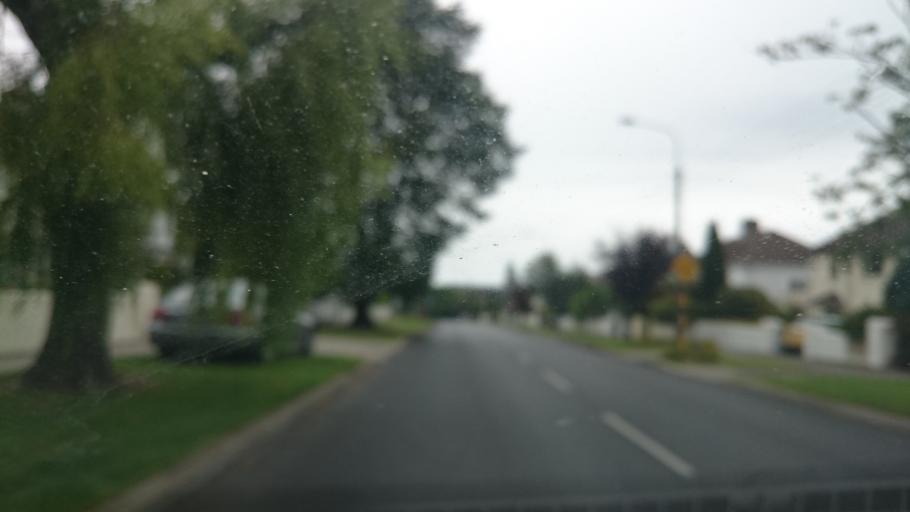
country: IE
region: Leinster
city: Mount Merrion
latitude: 53.2930
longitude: -6.2108
